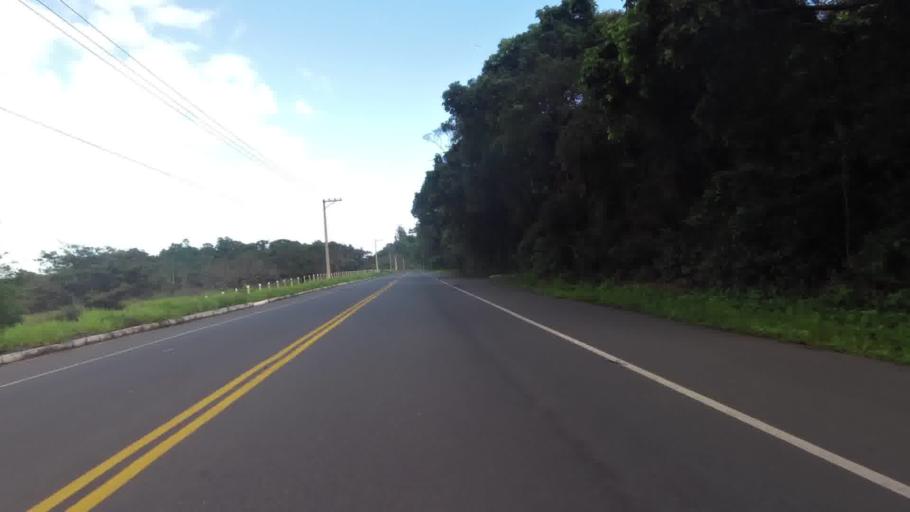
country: BR
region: Espirito Santo
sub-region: Piuma
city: Piuma
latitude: -20.8009
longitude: -40.6284
